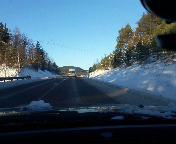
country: SE
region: Gaevleborg
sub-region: Ljusdals Kommun
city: Jaervsoe
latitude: 61.6692
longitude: 16.1472
